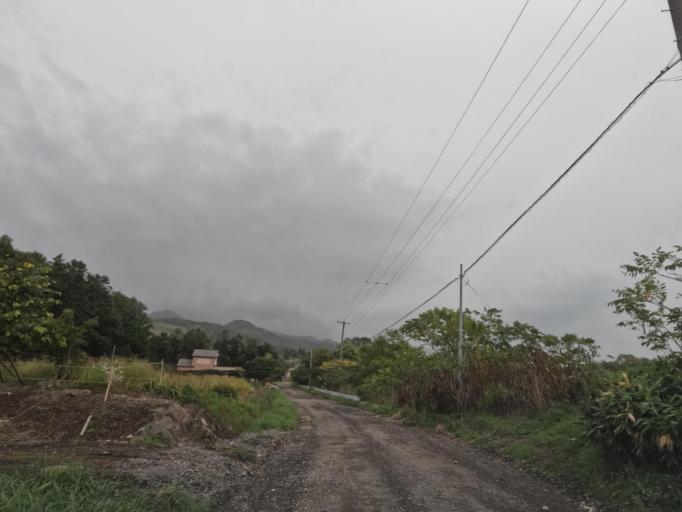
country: JP
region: Hokkaido
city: Date
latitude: 42.4542
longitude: 140.9088
